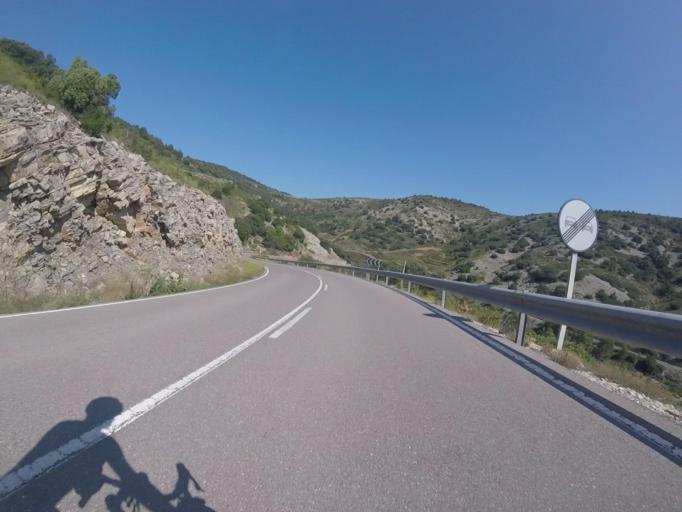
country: ES
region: Valencia
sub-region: Provincia de Castello
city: Benafigos
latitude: 40.2655
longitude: -0.2325
